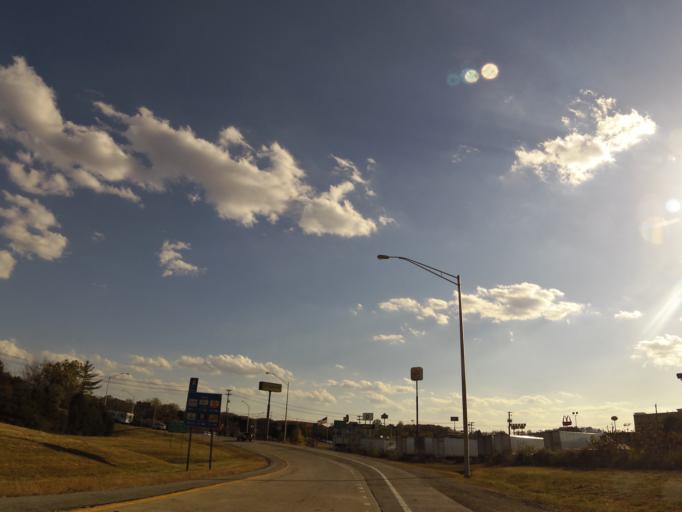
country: US
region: Tennessee
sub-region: Anderson County
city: Norris
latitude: 36.1672
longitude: -84.0841
